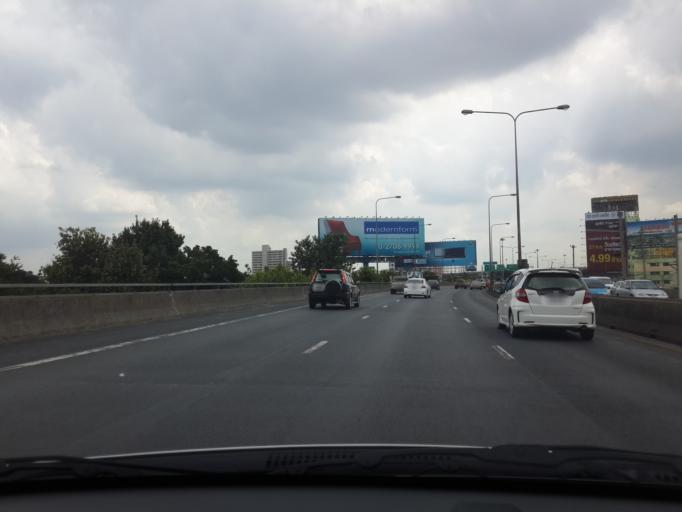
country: TH
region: Bangkok
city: Phra Khanong
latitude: 13.7064
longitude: 100.5880
